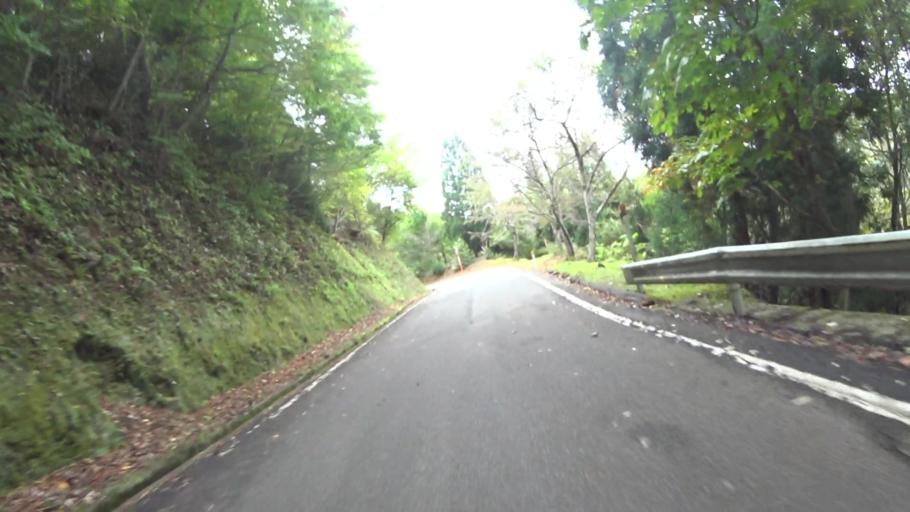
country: JP
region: Shiga Prefecture
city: Kitahama
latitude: 35.2749
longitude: 135.7285
